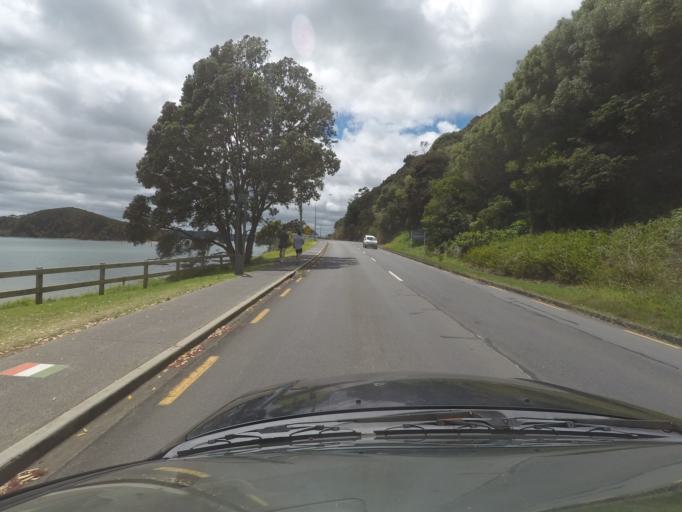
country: NZ
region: Northland
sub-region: Far North District
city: Paihia
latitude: -35.2789
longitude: 174.0880
